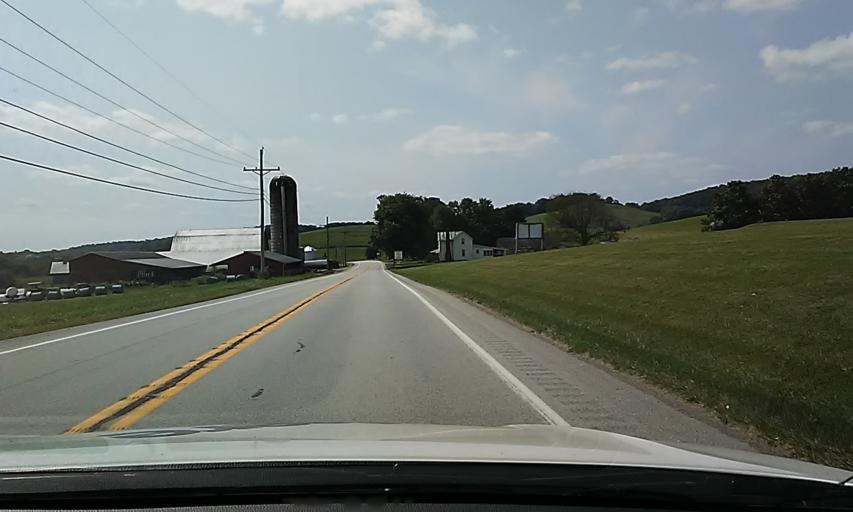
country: US
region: Pennsylvania
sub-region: Indiana County
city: Clymer
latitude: 40.7487
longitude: -79.0863
